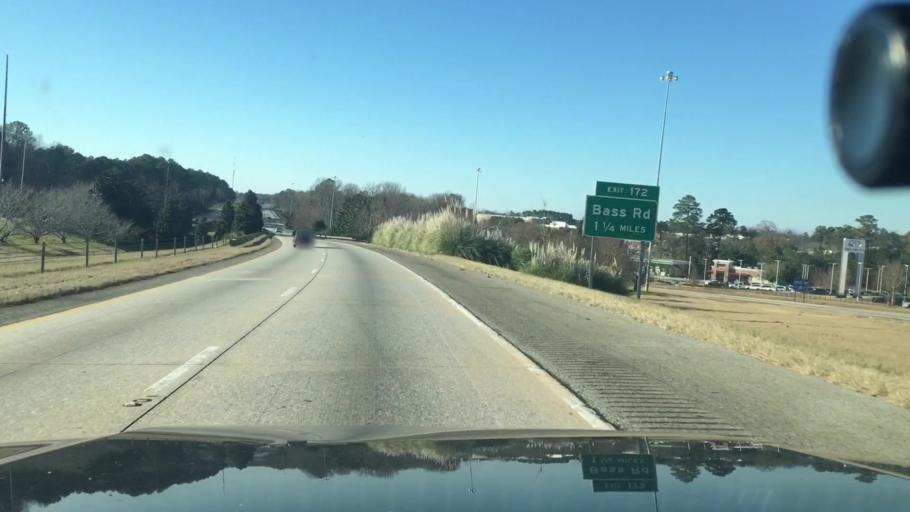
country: US
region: Georgia
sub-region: Bibb County
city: Macon
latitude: 32.9184
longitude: -83.7069
